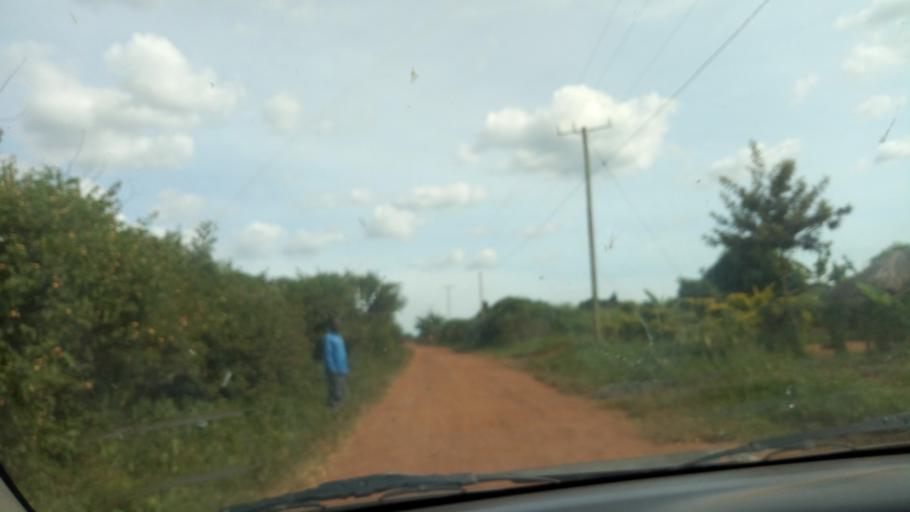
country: UG
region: Western Region
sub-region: Kiryandongo District
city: Kiryandongo
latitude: 1.8111
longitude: 31.9407
